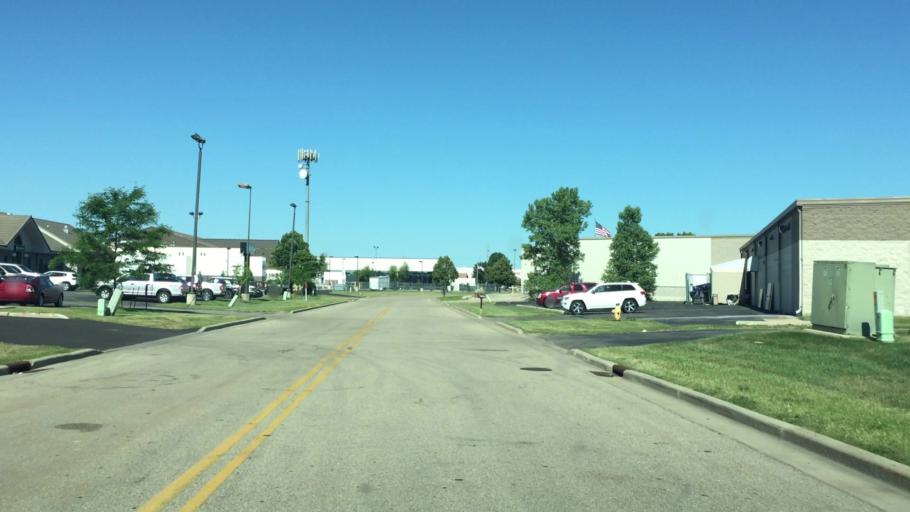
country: US
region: Wisconsin
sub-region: Outagamie County
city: Appleton
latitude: 44.2630
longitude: -88.4722
